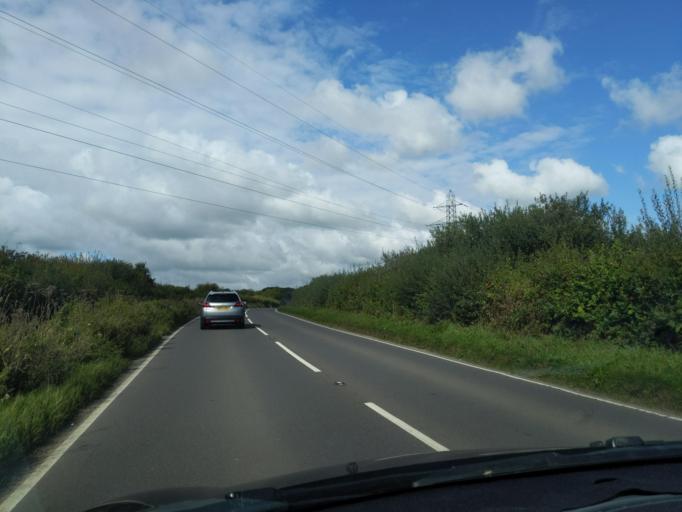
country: GB
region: England
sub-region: Devon
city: Holsworthy
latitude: 50.8385
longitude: -4.3400
